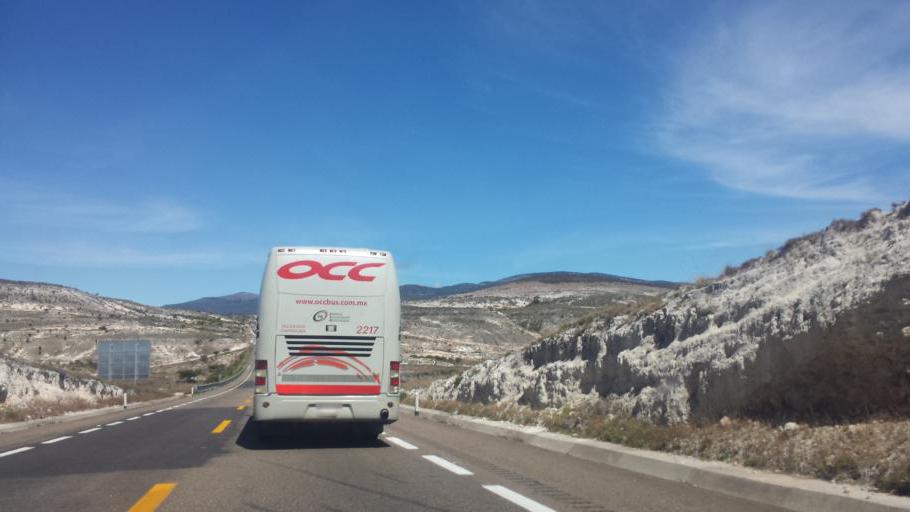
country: MX
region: Oaxaca
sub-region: Villa Tejupam de la Union
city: Villa Tejupam de la Union
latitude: 17.8988
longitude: -97.3682
